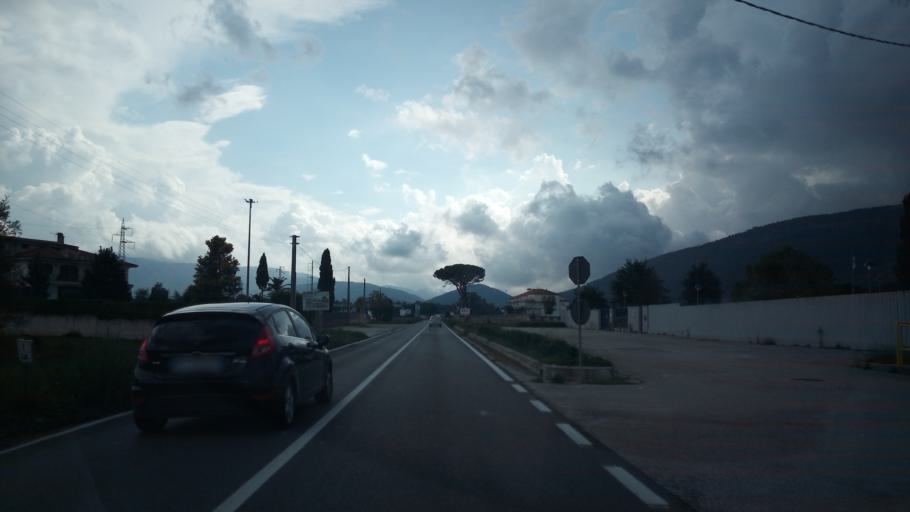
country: IT
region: Campania
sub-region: Provincia di Salerno
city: Buonabitacolo
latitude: 40.2908
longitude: 15.6420
